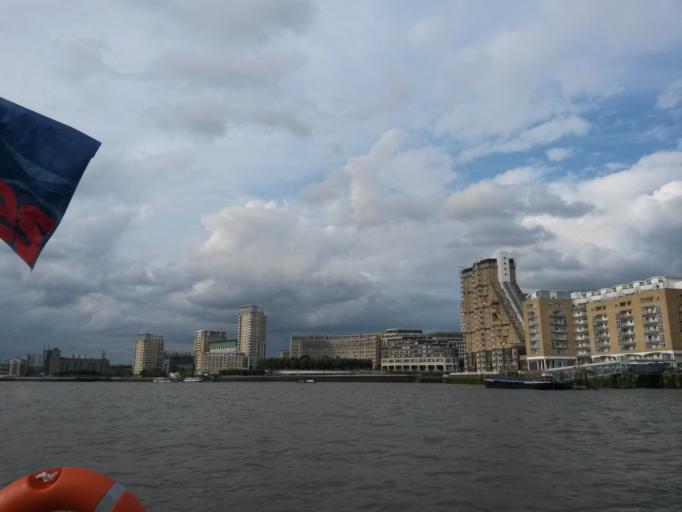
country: GB
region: England
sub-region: Greater London
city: Poplar
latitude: 51.5006
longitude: -0.0292
